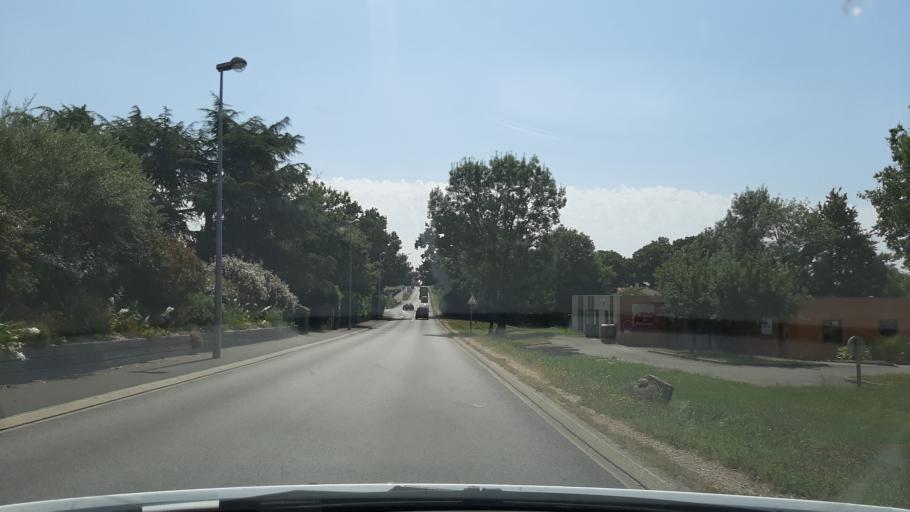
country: FR
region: Pays de la Loire
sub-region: Departement de la Vendee
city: Le Poire-sur-Vie
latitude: 46.7695
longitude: -1.5042
